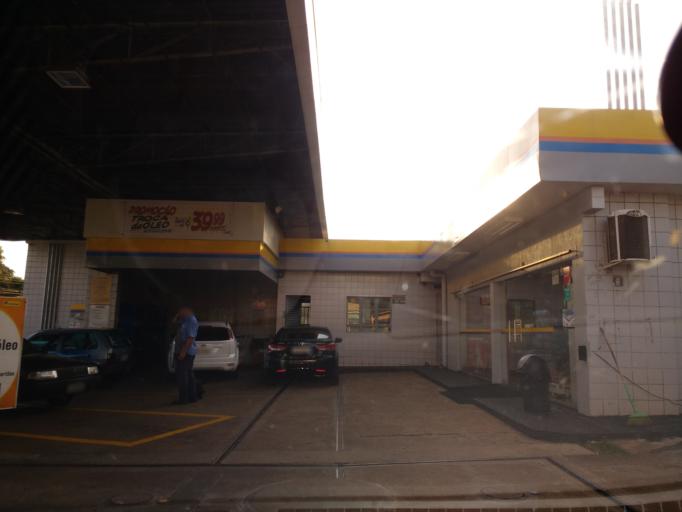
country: BR
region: Parana
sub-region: Londrina
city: Londrina
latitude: -23.2973
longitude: -51.1435
